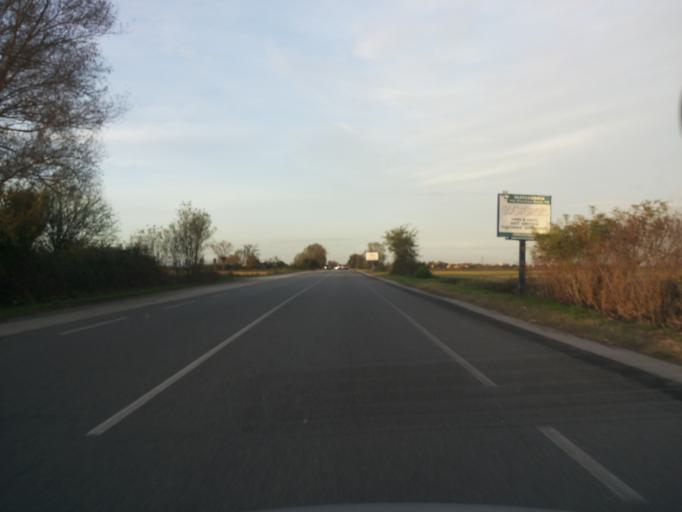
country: IT
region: Piedmont
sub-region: Provincia di Vercelli
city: Trino
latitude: 45.2116
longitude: 8.3051
